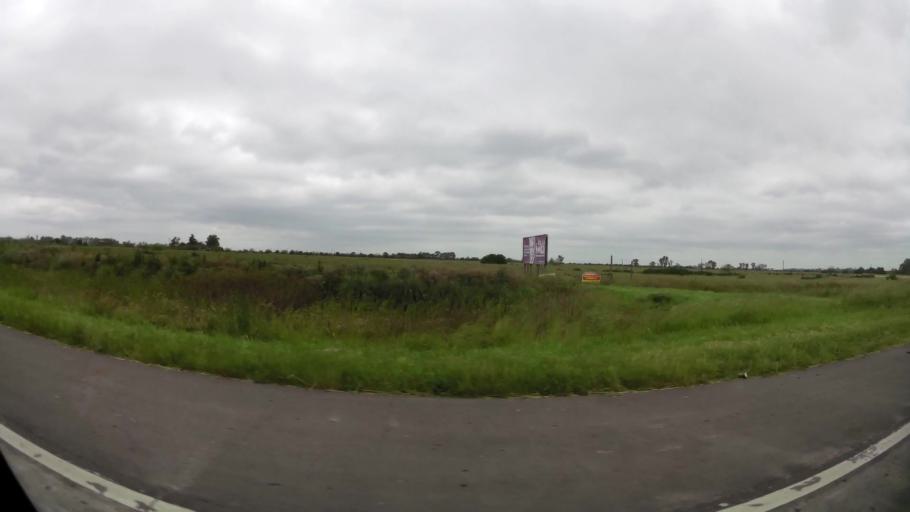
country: AR
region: Buenos Aires
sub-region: Partido de San Vicente
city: San Vicente
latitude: -35.0291
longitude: -58.3661
